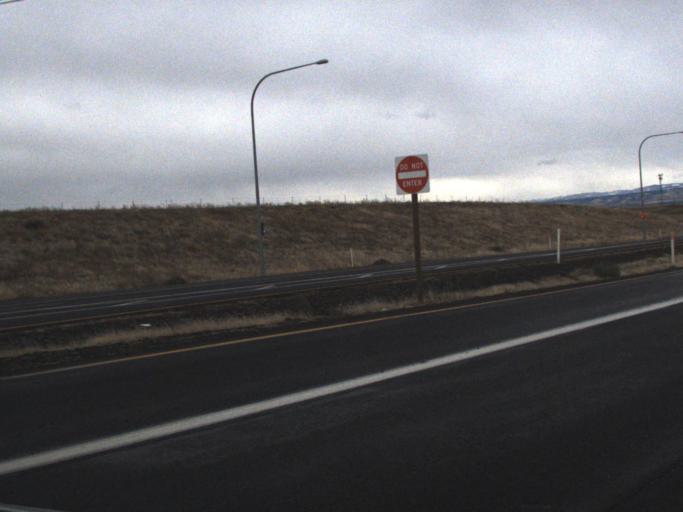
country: US
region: Washington
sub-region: Walla Walla County
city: Garrett
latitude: 46.0489
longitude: -118.4900
